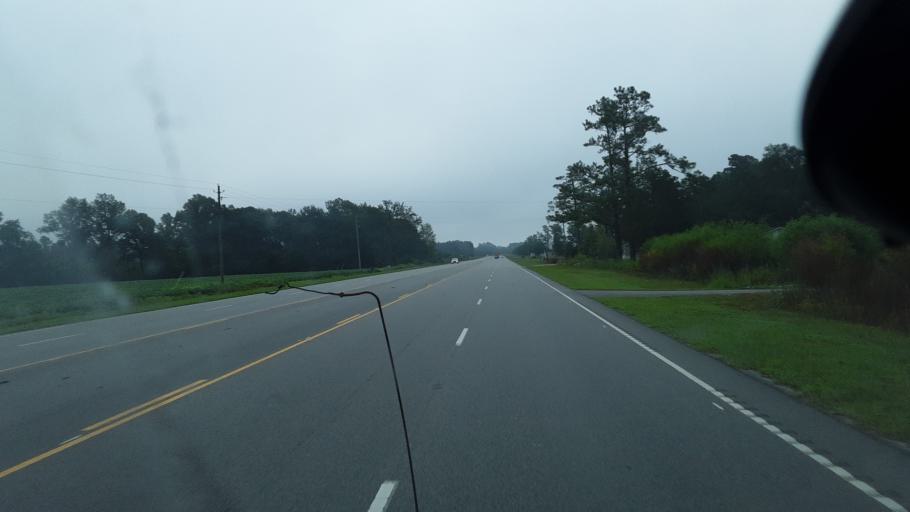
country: US
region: South Carolina
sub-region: Florence County
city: Johnsonville
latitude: 33.8825
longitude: -79.4691
